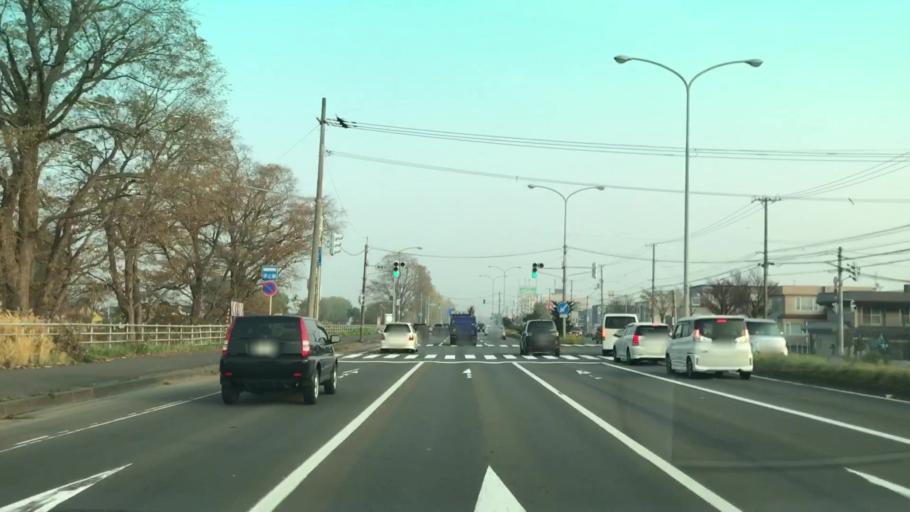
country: JP
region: Hokkaido
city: Ishikari
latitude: 43.1534
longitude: 141.3516
